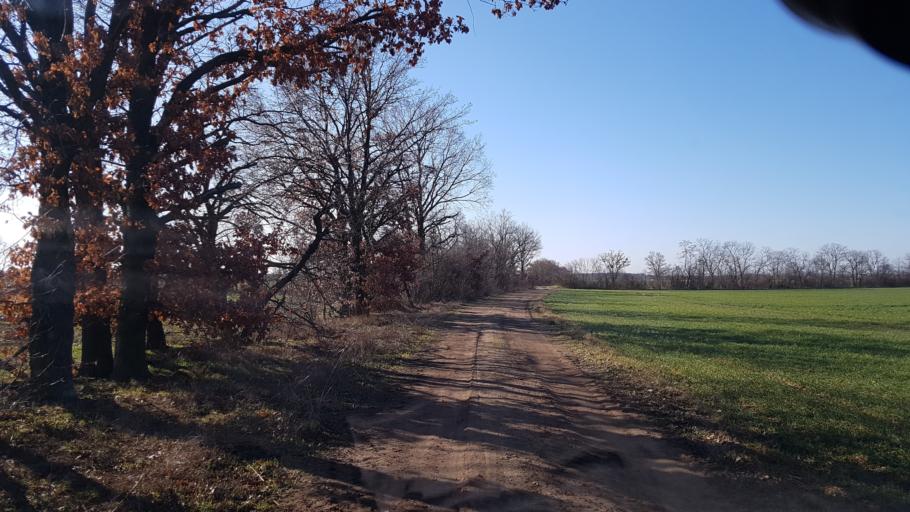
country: DE
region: Brandenburg
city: Falkenberg
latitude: 51.5102
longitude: 13.2474
